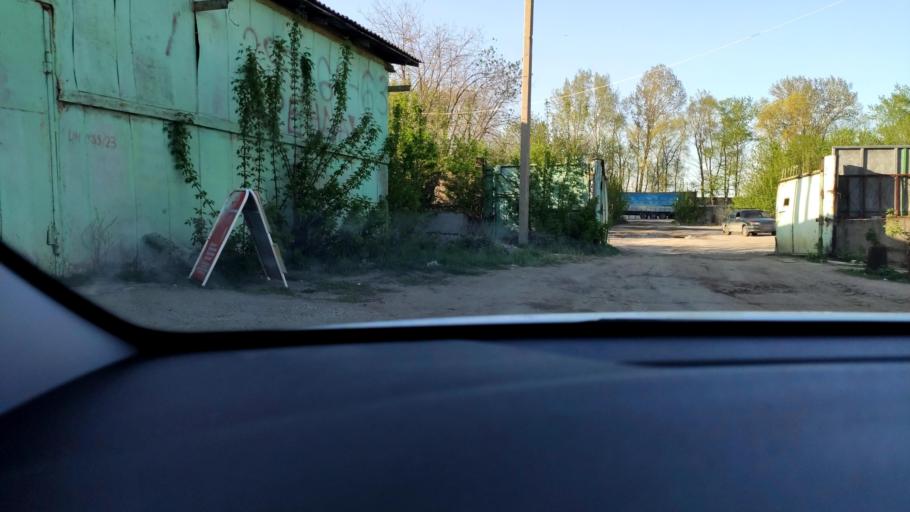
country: RU
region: Tatarstan
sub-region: Gorod Kazan'
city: Kazan
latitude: 55.7331
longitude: 49.1010
